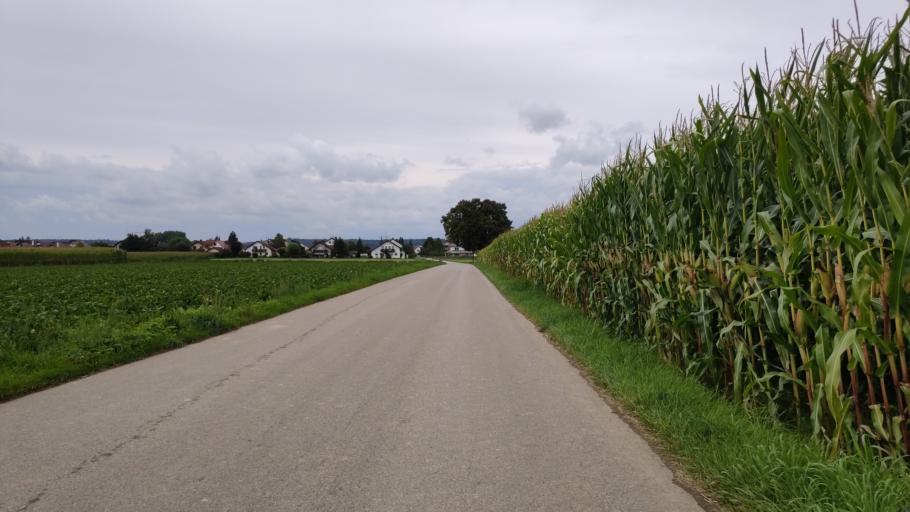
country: DE
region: Bavaria
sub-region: Swabia
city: Wehringen
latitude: 48.2419
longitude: 10.8073
